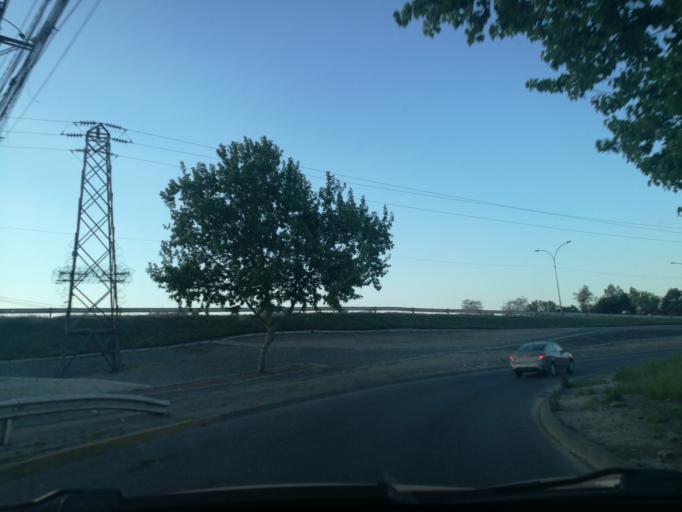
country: CL
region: O'Higgins
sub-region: Provincia de Cachapoal
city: Rancagua
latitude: -34.1792
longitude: -70.7324
